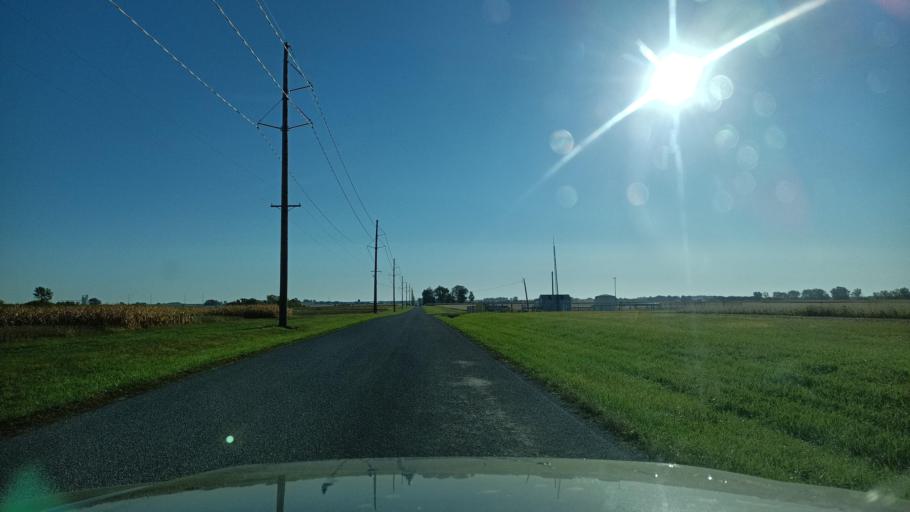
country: US
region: Illinois
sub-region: Champaign County
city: Savoy
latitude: 40.0543
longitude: -88.2364
